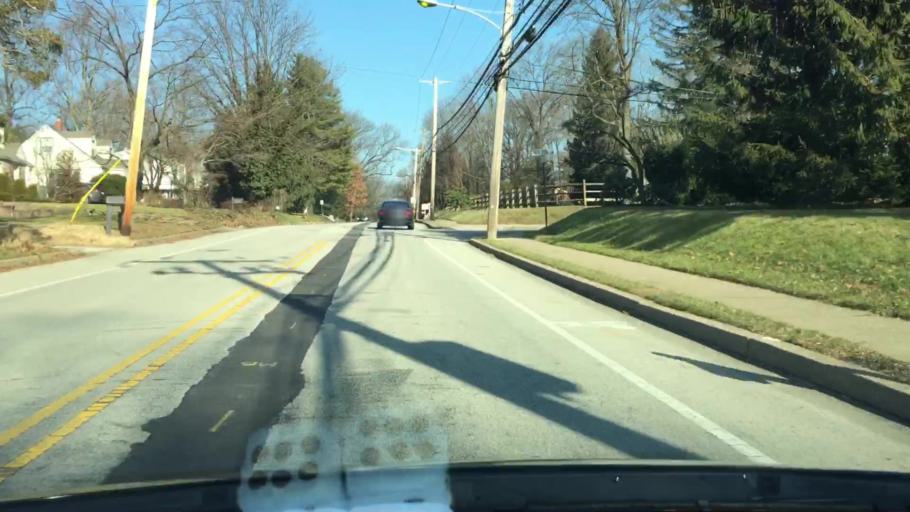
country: US
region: Pennsylvania
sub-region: Delaware County
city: Wayne
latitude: 40.0582
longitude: -75.4064
